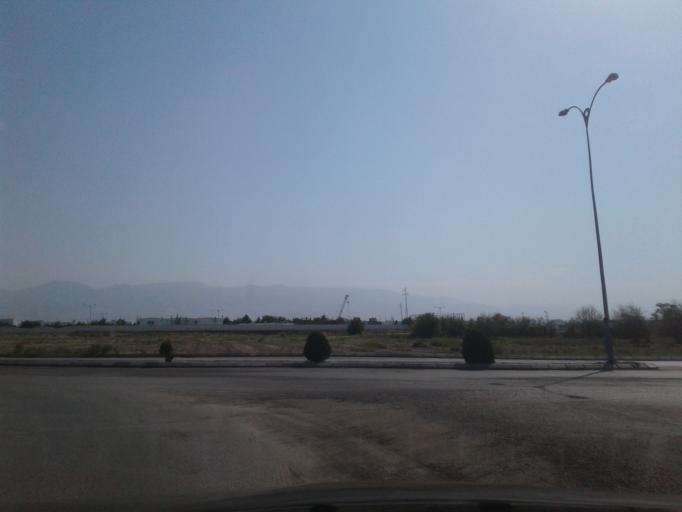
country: TM
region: Ahal
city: Ashgabat
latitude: 37.9699
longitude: 58.4224
